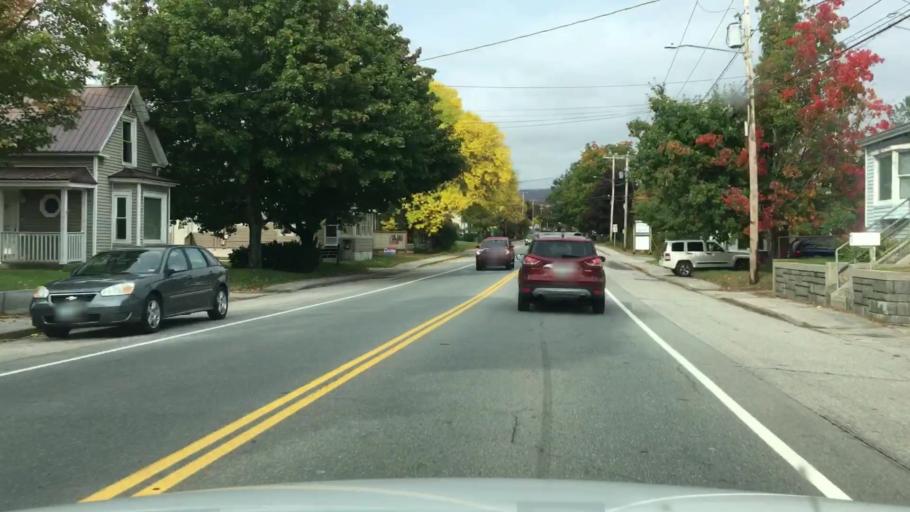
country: US
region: New Hampshire
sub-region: Coos County
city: Gorham
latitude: 44.3868
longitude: -71.1679
